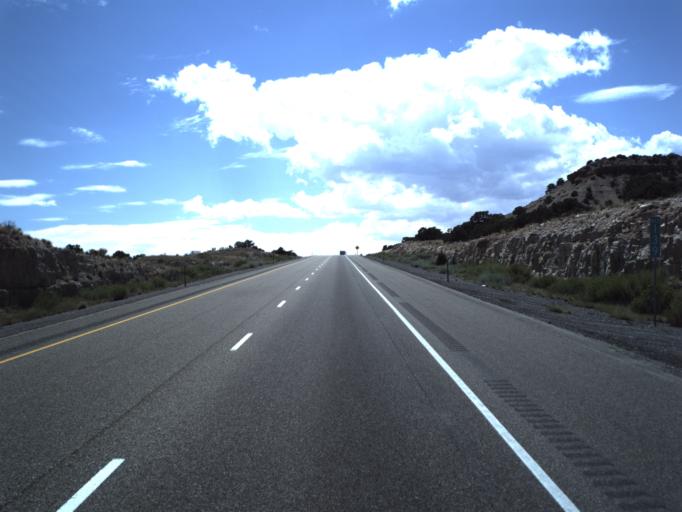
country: US
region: Utah
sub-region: Emery County
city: Castle Dale
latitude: 38.9091
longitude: -110.5283
